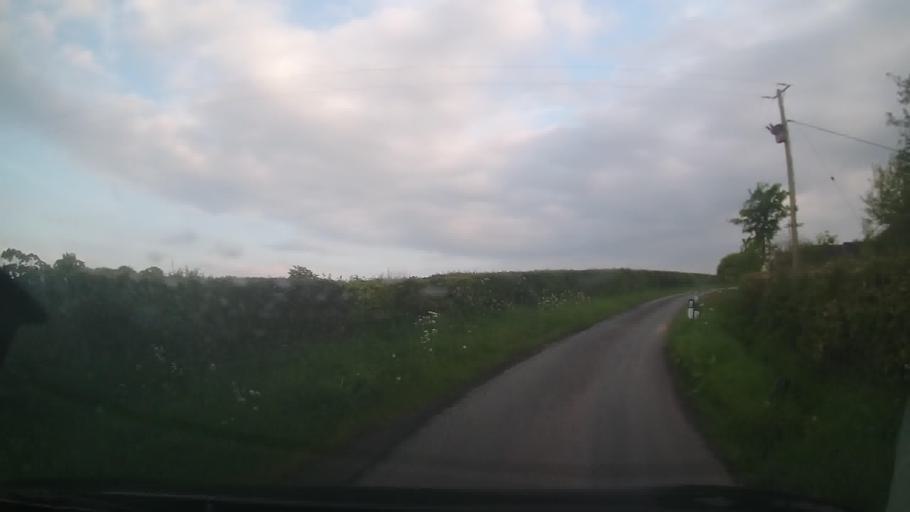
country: GB
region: England
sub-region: Shropshire
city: Ellesmere
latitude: 52.9376
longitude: -2.8611
